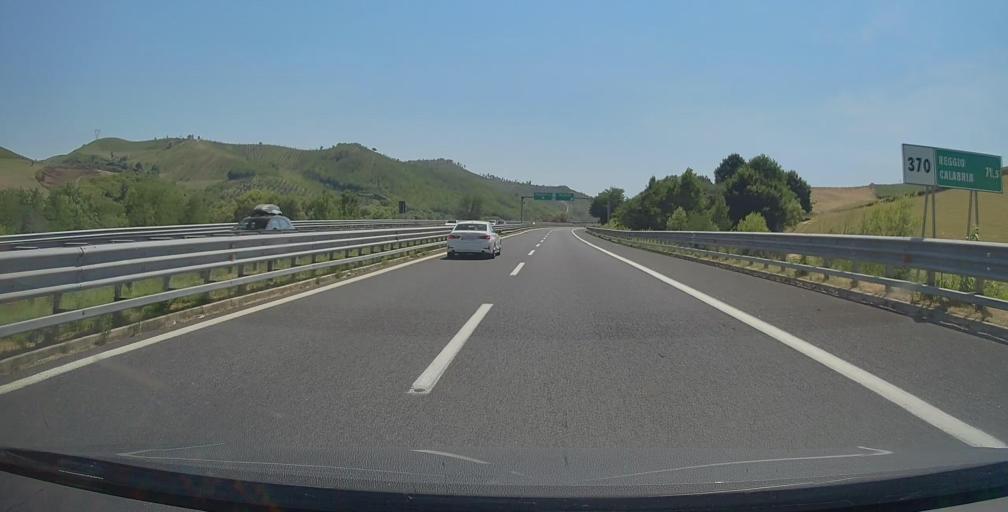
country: IT
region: Calabria
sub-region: Provincia di Vibo-Valentia
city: Paravati
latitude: 38.5690
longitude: 16.0880
